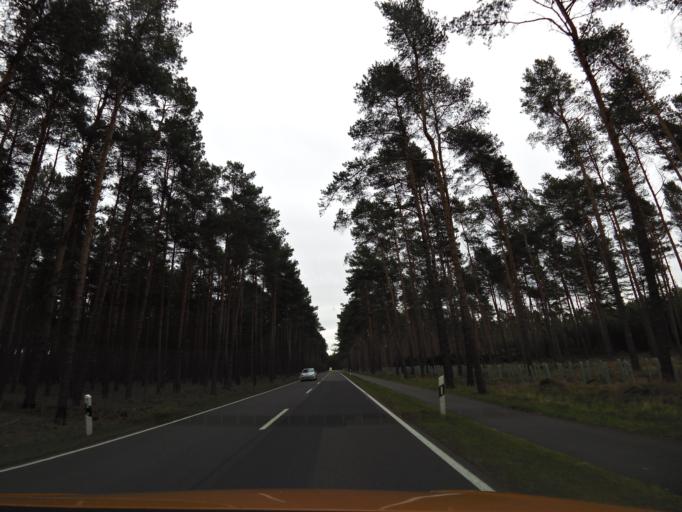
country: DE
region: Brandenburg
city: Borkheide
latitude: 52.2031
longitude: 12.8442
